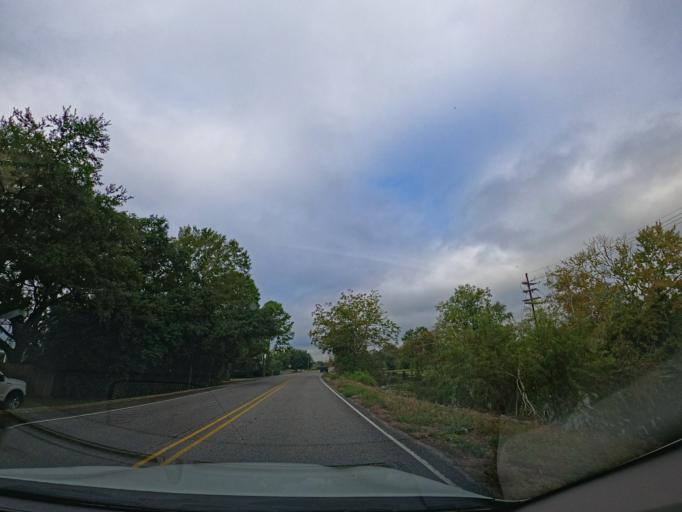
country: US
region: Louisiana
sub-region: Terrebonne Parish
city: Houma
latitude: 29.5736
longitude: -90.7584
